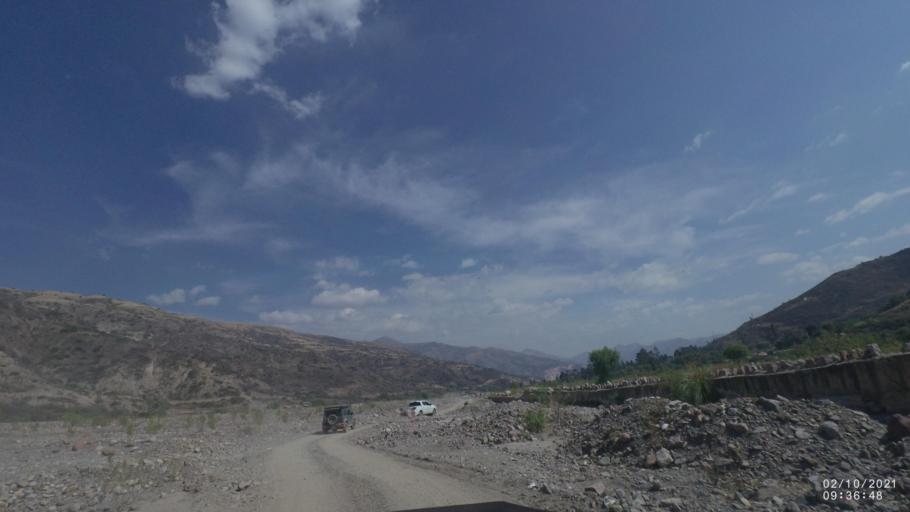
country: BO
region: Cochabamba
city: Irpa Irpa
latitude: -17.8321
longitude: -66.3222
